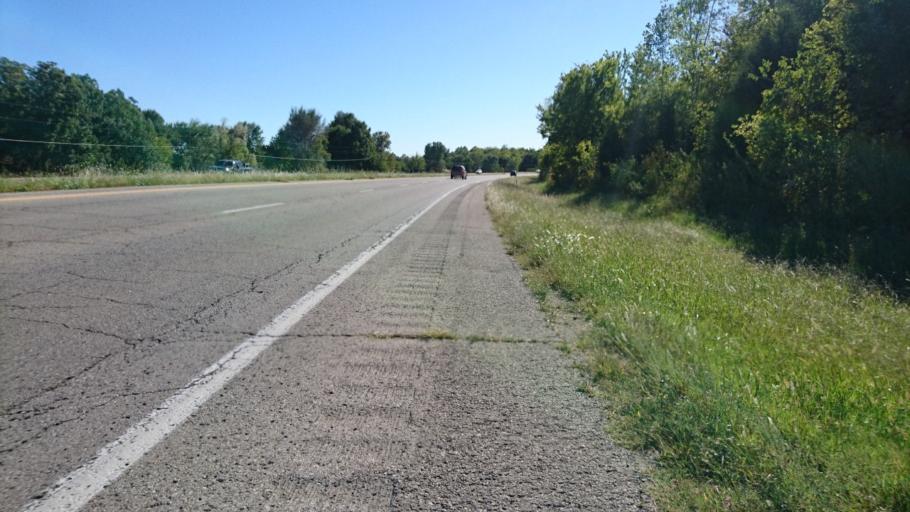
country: US
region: Oklahoma
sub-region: Rogers County
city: Claremore
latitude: 36.3717
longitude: -95.5639
